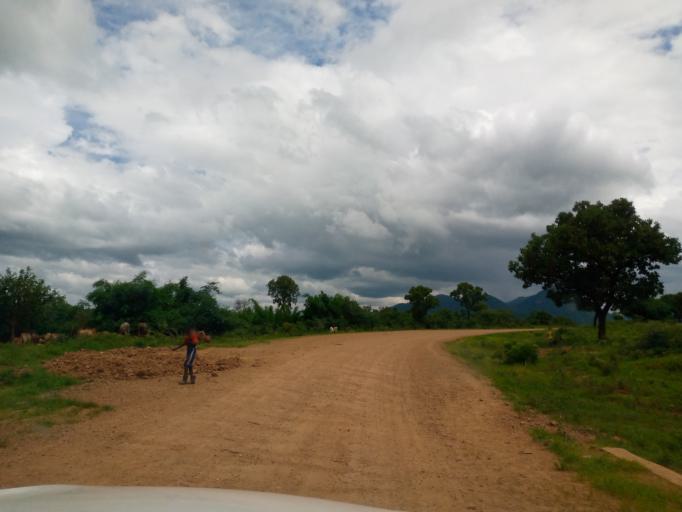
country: ET
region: Oromiya
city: Mendi
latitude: 10.2023
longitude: 35.0929
